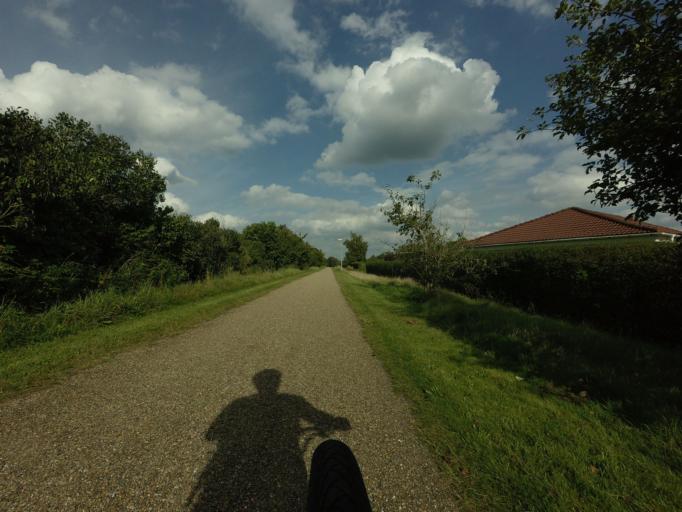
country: DK
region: Central Jutland
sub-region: Herning Kommune
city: Sunds
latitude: 56.2332
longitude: 9.0846
